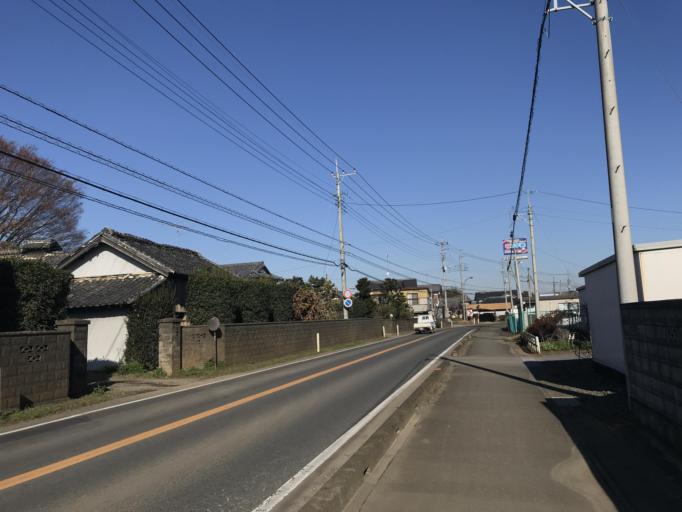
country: JP
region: Tochigi
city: Oyama
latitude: 36.2592
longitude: 139.8384
